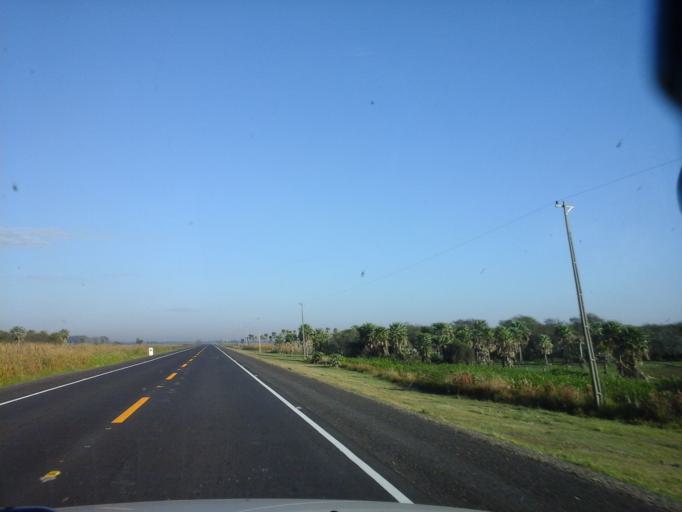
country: PY
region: Neembucu
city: Pilar
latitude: -26.8633
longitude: -57.8450
